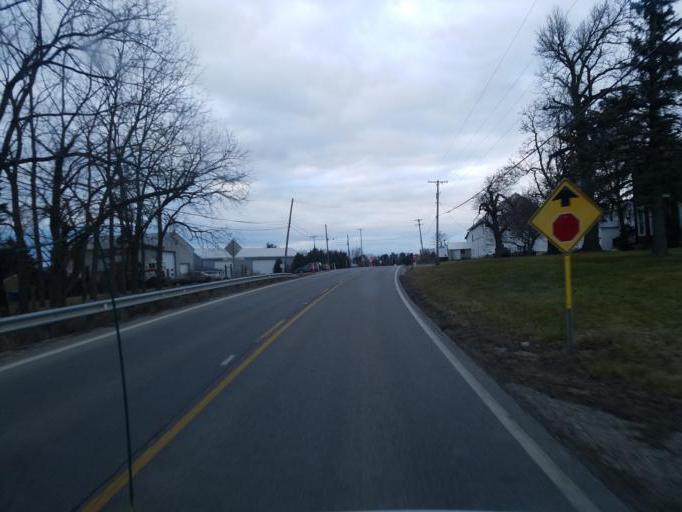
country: US
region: Ohio
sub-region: Delaware County
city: Delaware
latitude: 40.3190
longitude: -83.1235
